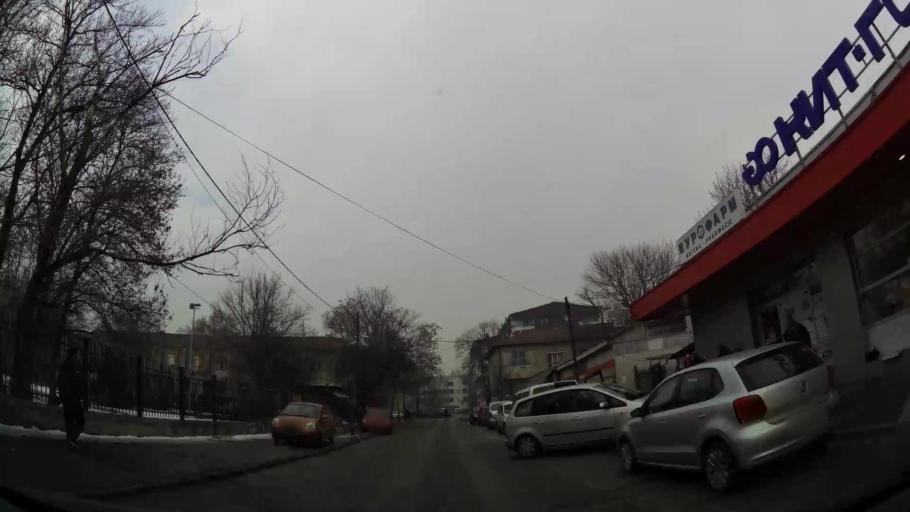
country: MK
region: Cair
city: Cair
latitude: 42.0037
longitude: 21.4671
